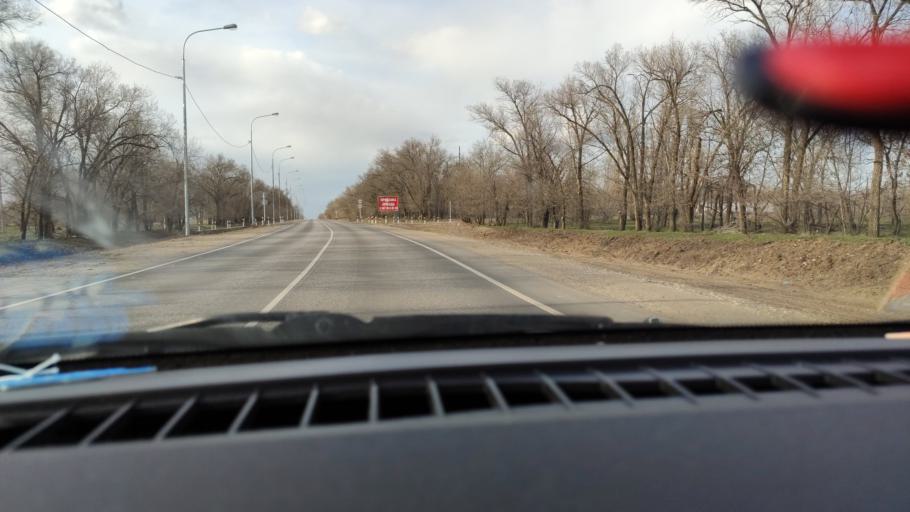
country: RU
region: Saratov
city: Krasnoarmeysk
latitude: 51.0923
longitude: 45.9564
